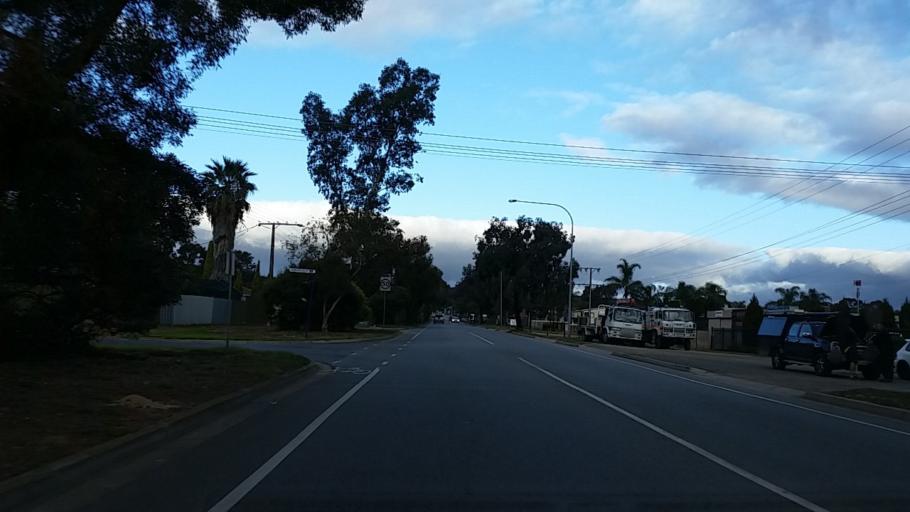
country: AU
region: South Australia
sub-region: Salisbury
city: Salisbury
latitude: -34.7627
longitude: 138.6637
